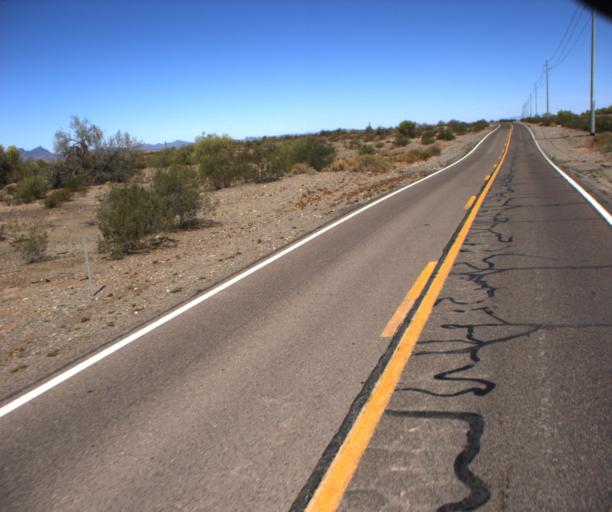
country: US
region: Arizona
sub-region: La Paz County
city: Salome
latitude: 33.7609
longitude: -113.7820
